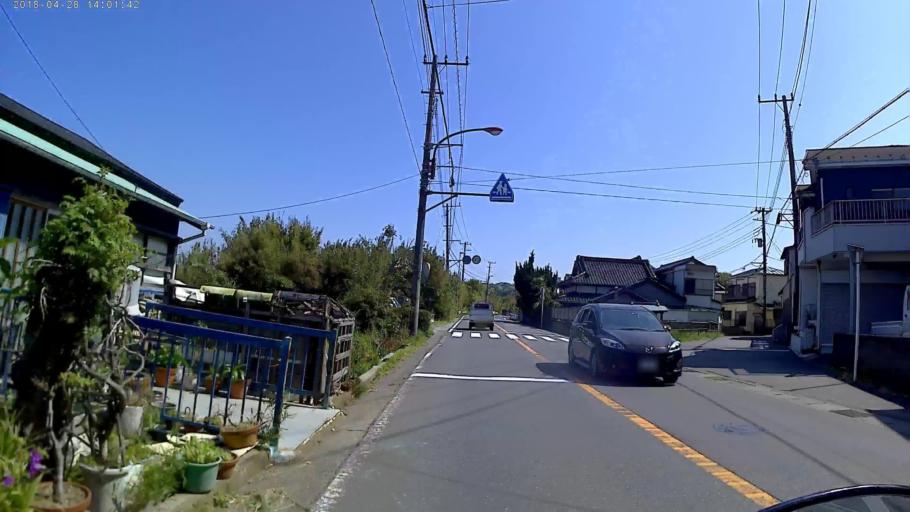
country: JP
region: Kanagawa
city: Miura
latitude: 35.1665
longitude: 139.6595
